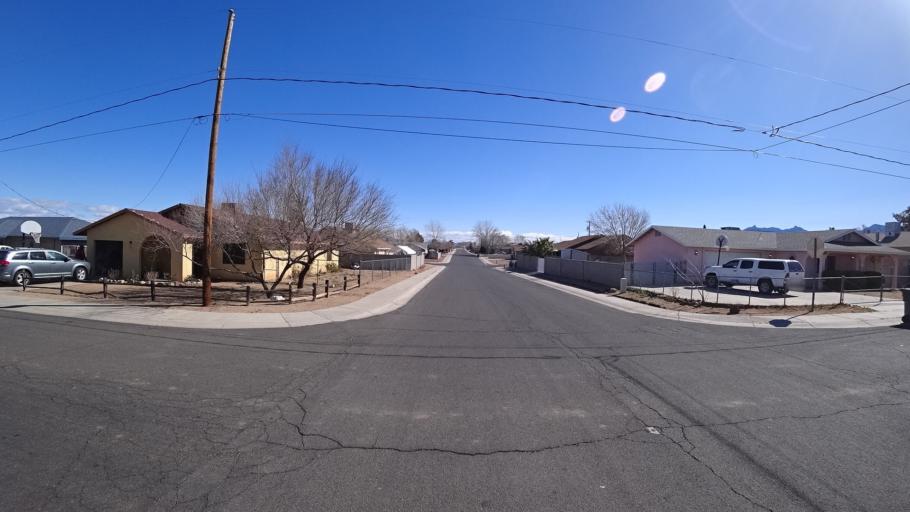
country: US
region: Arizona
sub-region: Mohave County
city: New Kingman-Butler
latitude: 35.2194
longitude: -113.9993
